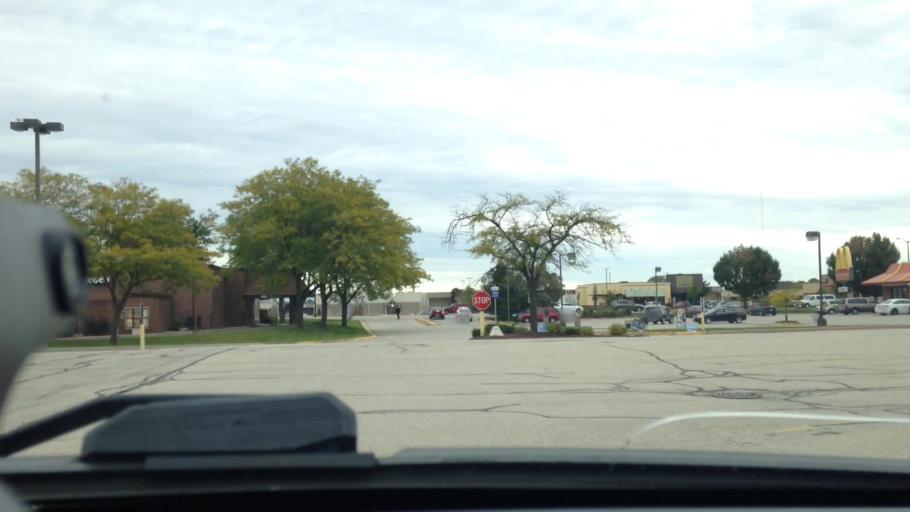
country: US
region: Wisconsin
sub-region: Fond du Lac County
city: North Fond du Lac
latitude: 43.7830
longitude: -88.4759
